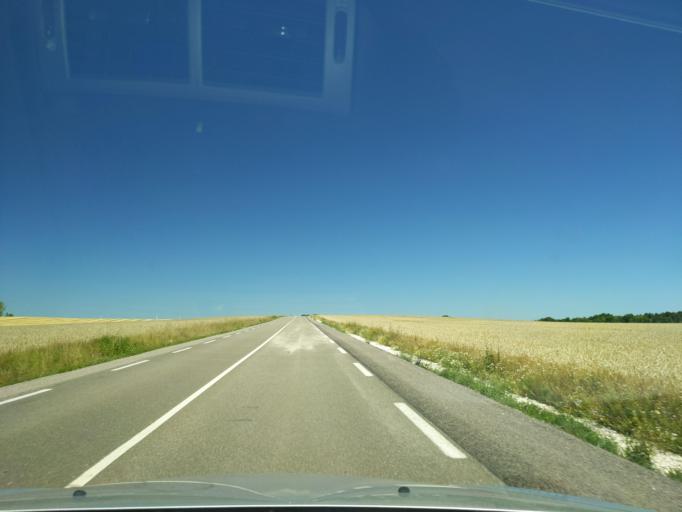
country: FR
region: Bourgogne
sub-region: Departement de la Cote-d'Or
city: Is-sur-Tille
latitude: 47.4856
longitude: 5.0875
